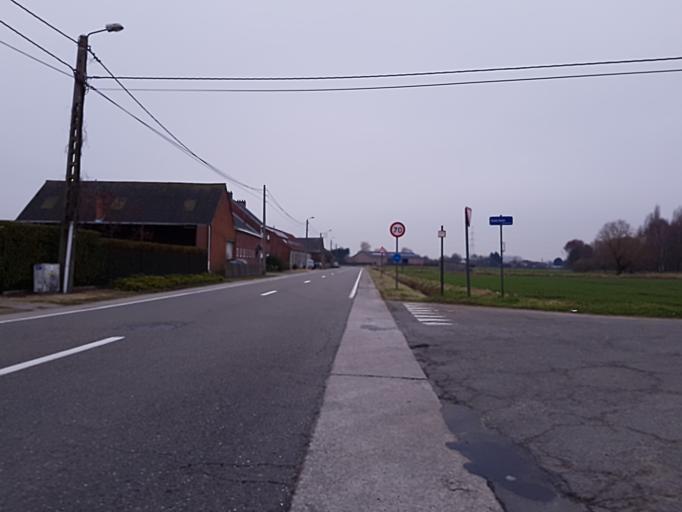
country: BE
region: Flanders
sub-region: Provincie Vlaams-Brabant
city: Kapelle-op-den-Bos
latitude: 51.0363
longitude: 4.3919
